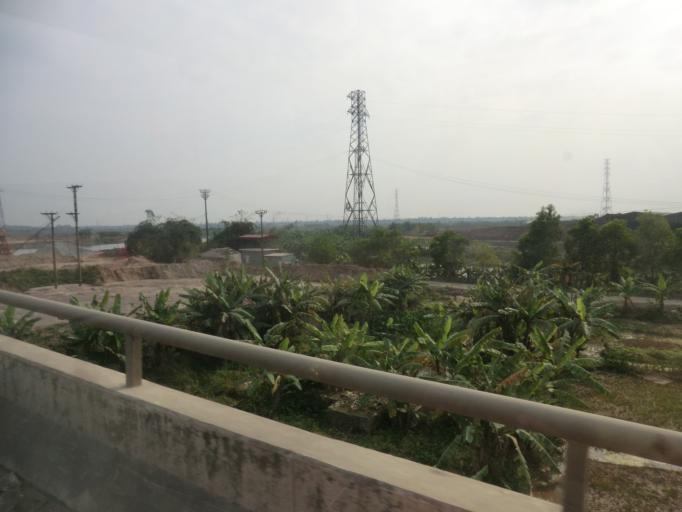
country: VN
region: Hai Phong
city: An Lao
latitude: 20.7756
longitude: 106.5037
